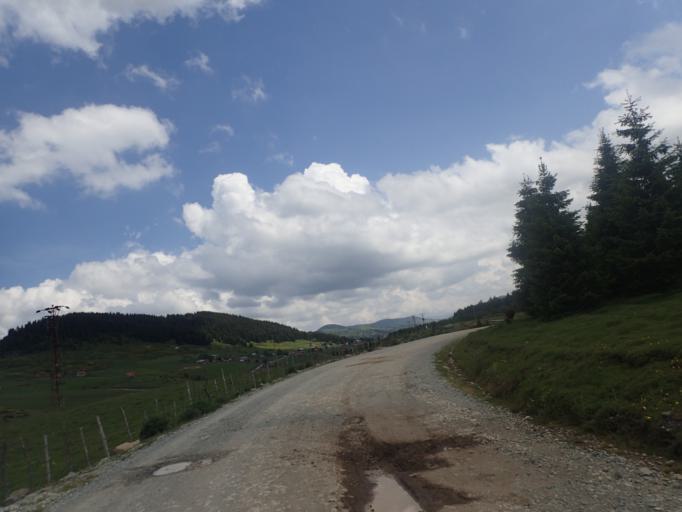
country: TR
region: Ordu
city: Topcam
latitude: 40.6826
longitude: 37.9372
